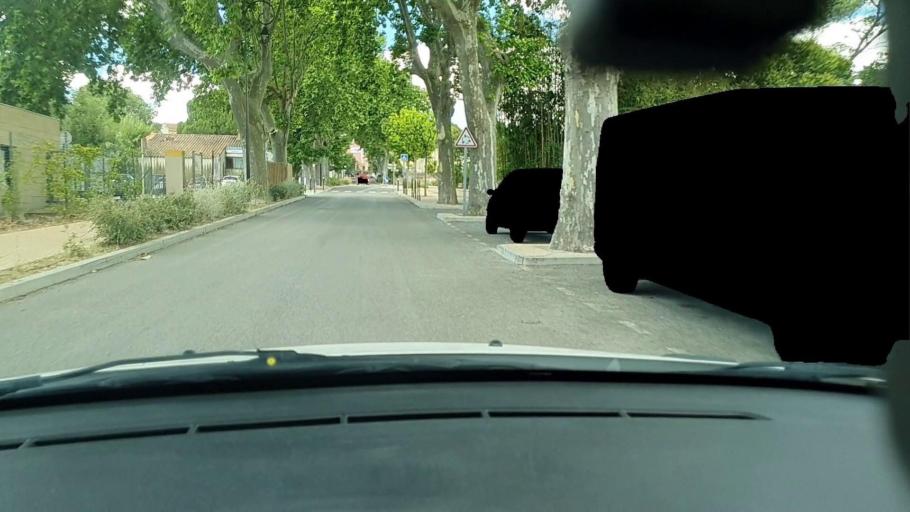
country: FR
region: Languedoc-Roussillon
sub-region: Departement du Gard
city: Cabrieres
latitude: 43.9536
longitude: 4.4803
